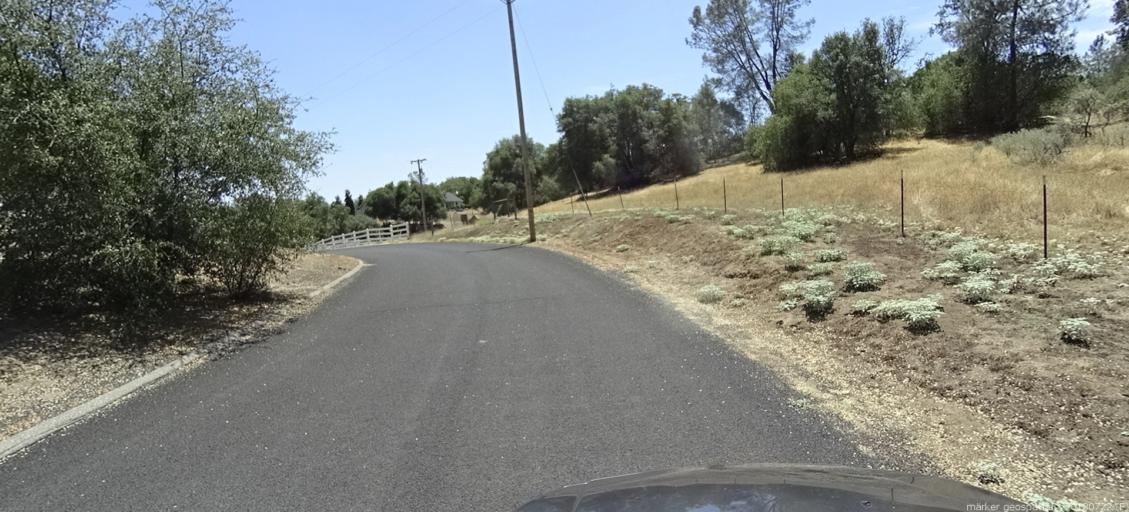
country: US
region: California
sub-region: Madera County
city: Yosemite Lakes
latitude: 37.2178
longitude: -119.7364
